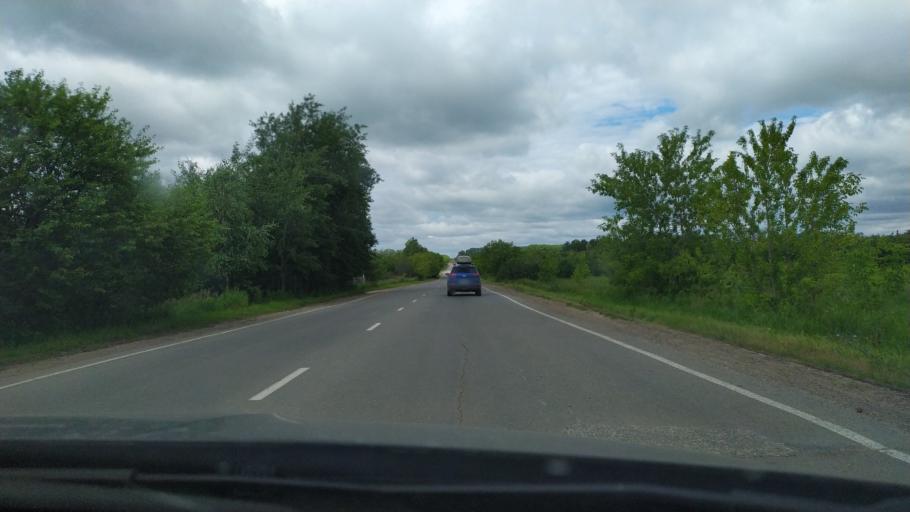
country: RU
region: Perm
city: Kondratovo
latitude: 57.9291
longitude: 56.1054
